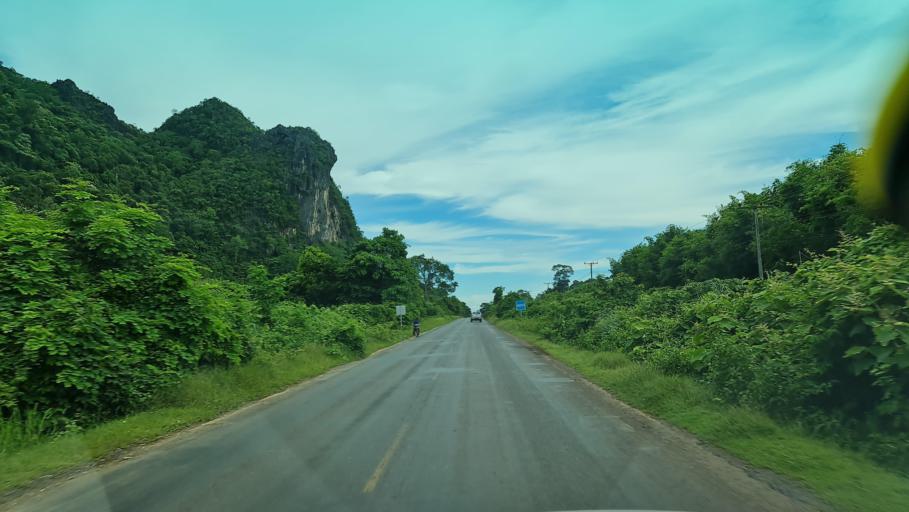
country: TH
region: Nakhon Phanom
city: Ban Phaeng
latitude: 18.0085
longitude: 104.3158
